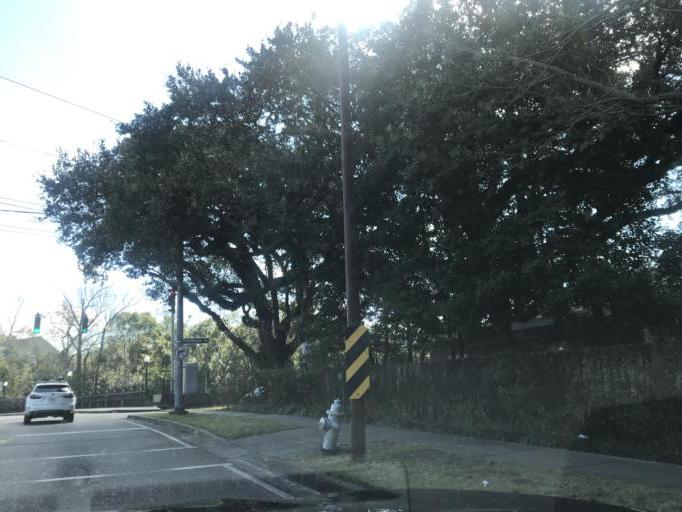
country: US
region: Louisiana
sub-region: Jefferson Parish
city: Metairie
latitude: 29.9795
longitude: -90.1256
